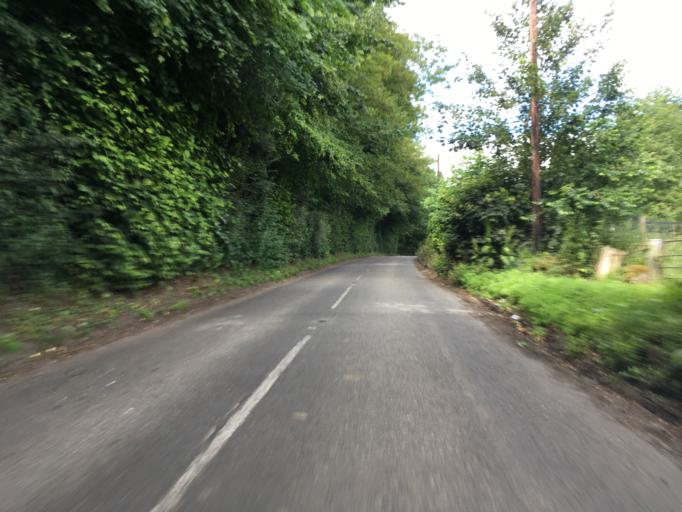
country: GB
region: England
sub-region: West Berkshire
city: Wickham
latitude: 51.4675
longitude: -1.4391
